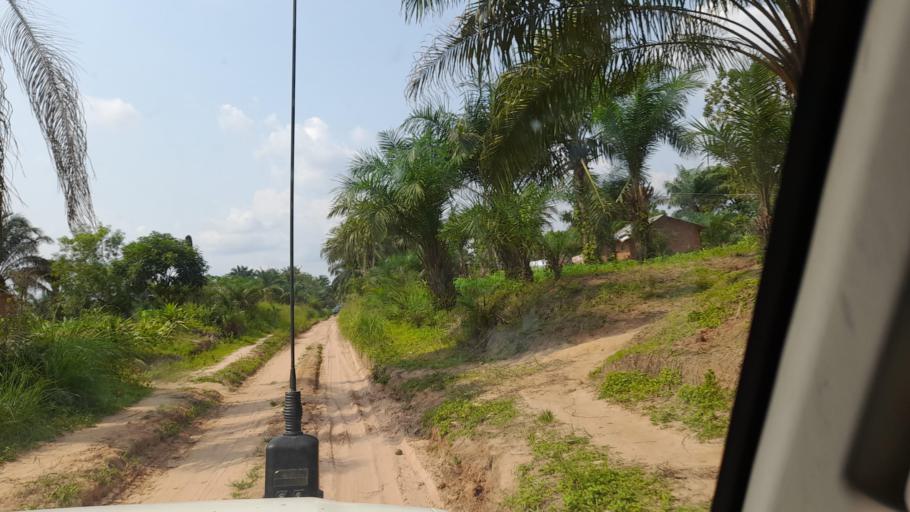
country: CD
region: Kasai-Occidental
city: Kananga
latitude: -5.9196
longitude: 22.4781
